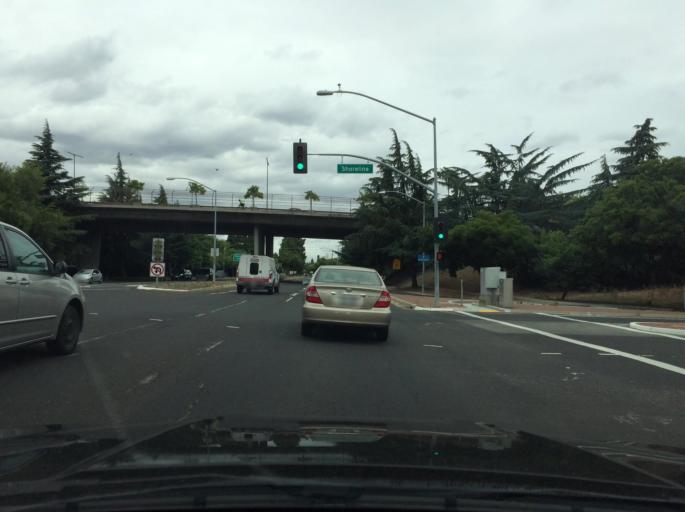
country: US
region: California
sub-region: Santa Clara County
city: Mountain View
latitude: 37.3970
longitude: -122.0809
